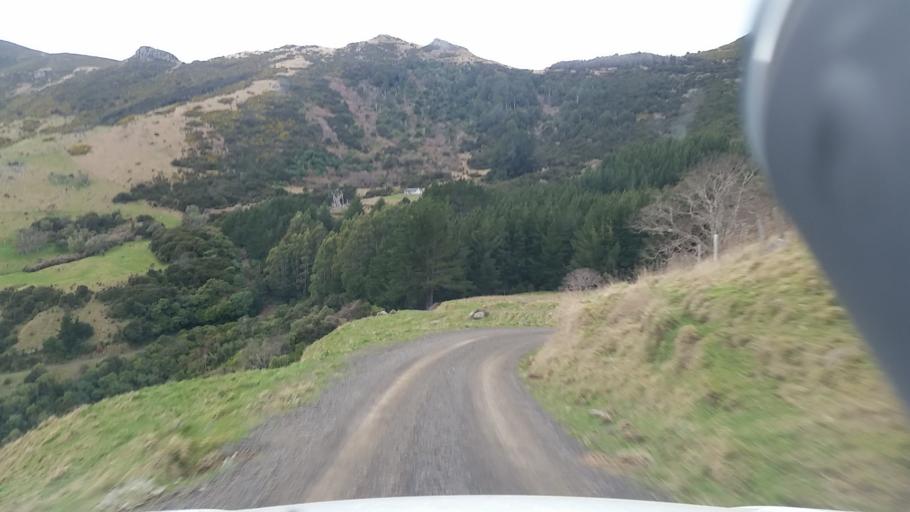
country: NZ
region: Canterbury
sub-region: Christchurch City
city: Christchurch
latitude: -43.8232
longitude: 172.9849
